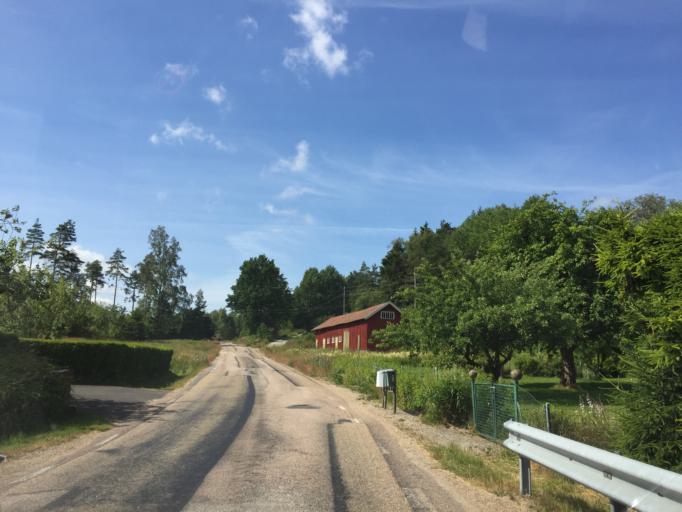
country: SE
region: Vaestra Goetaland
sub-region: Orust
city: Henan
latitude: 58.3076
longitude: 11.6696
